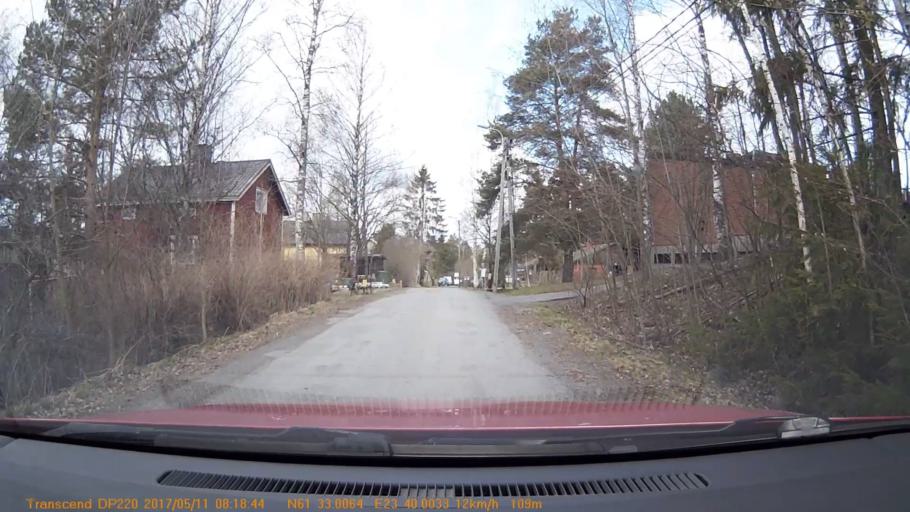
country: FI
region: Pirkanmaa
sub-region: Tampere
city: Yloejaervi
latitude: 61.5501
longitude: 23.6668
